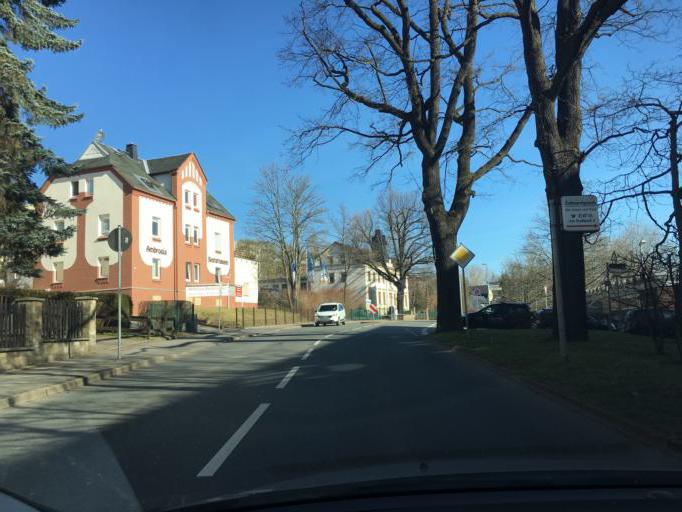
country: DE
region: Saxony
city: Neukirchen
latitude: 50.8061
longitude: 12.8974
